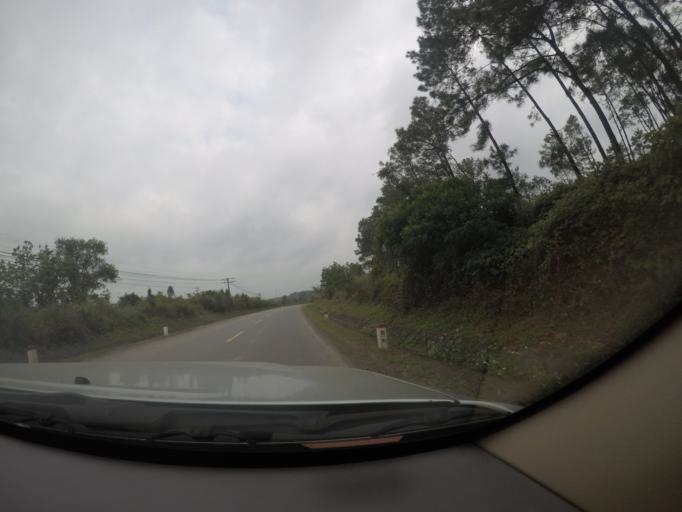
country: VN
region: Quang Binh
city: Quan Hau
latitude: 17.3940
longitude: 106.6107
